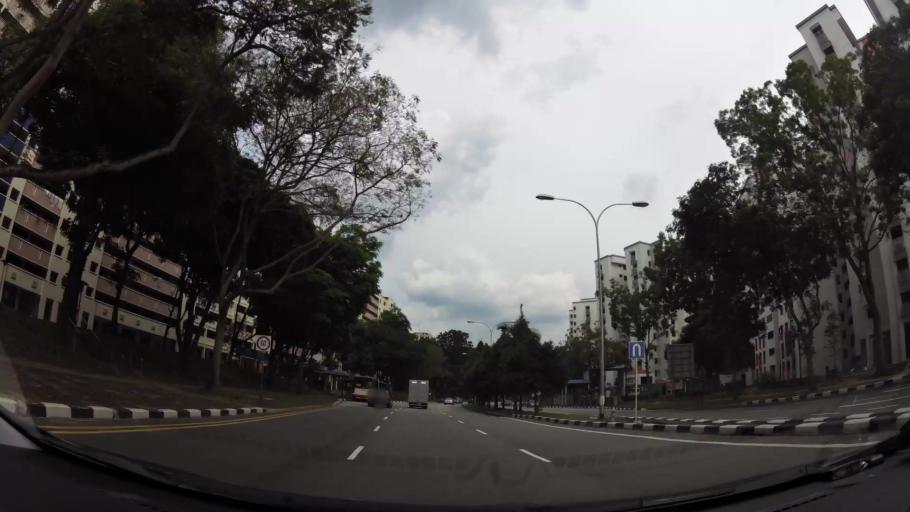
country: MY
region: Johor
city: Johor Bahru
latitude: 1.4351
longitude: 103.7893
